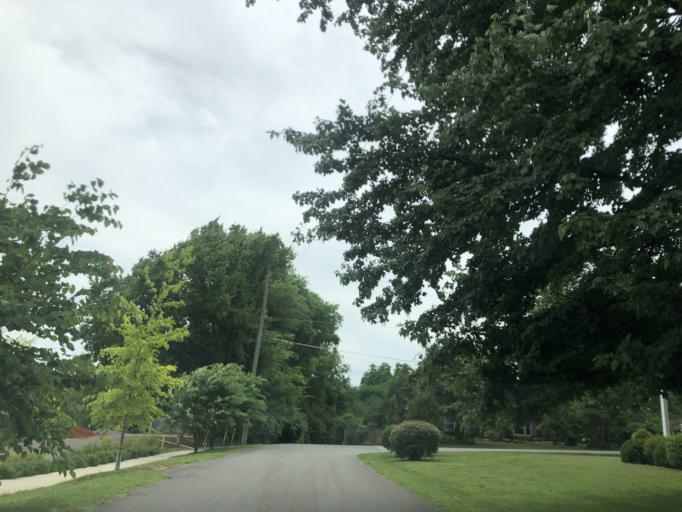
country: US
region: Tennessee
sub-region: Davidson County
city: Oak Hill
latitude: 36.1058
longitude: -86.7927
